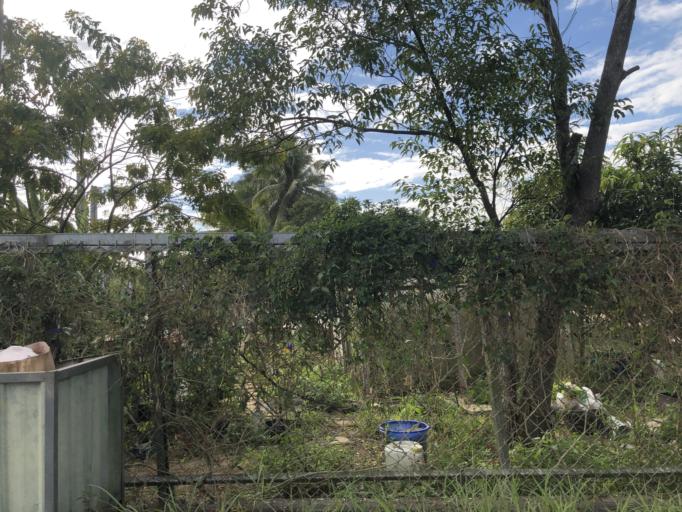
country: TW
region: Taiwan
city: Yujing
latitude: 23.0132
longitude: 120.4170
